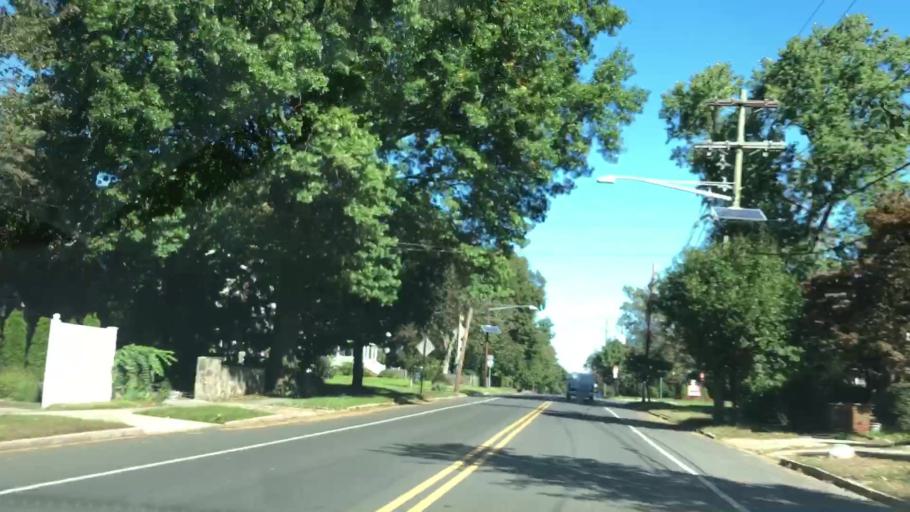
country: US
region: New Jersey
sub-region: Essex County
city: Glen Ridge
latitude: 40.8033
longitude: -74.2191
